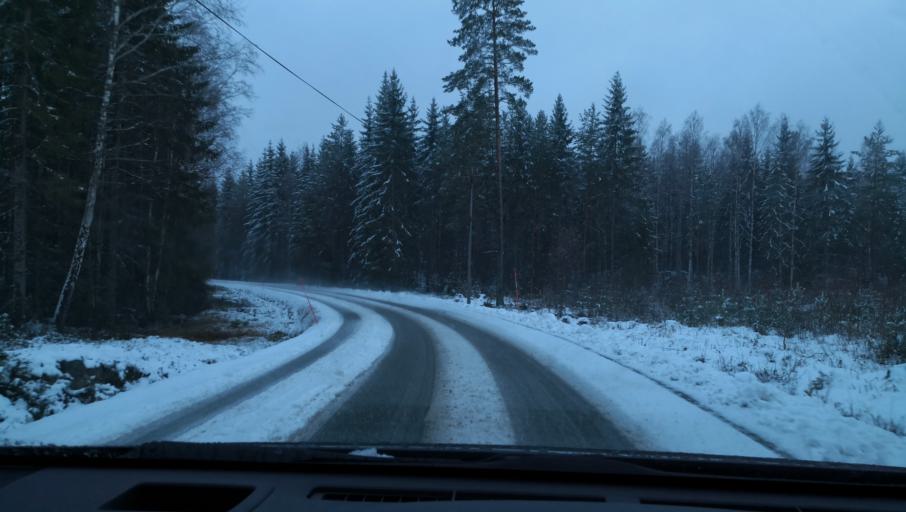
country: SE
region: Vaestmanland
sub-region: Kopings Kommun
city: Kolsva
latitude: 59.5840
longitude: 15.8036
